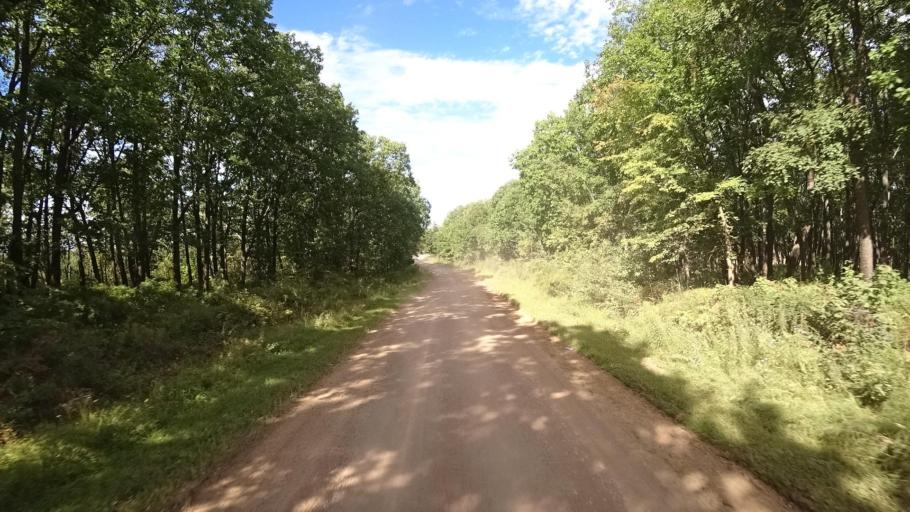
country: RU
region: Primorskiy
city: Yakovlevka
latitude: 44.4142
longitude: 133.5702
